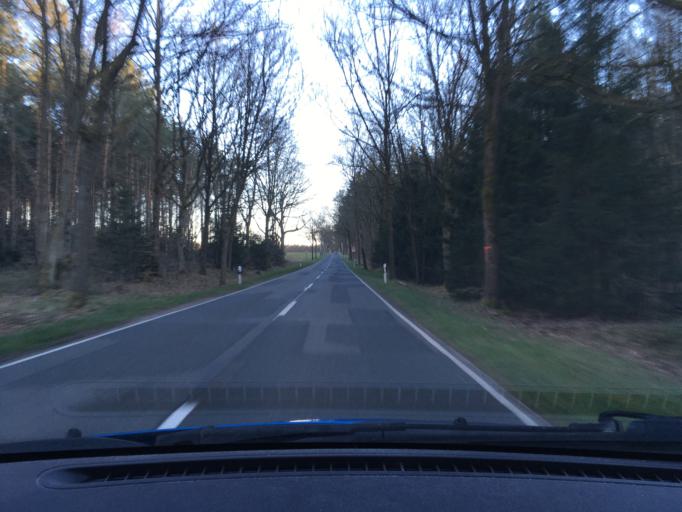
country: DE
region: Lower Saxony
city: Bleckede
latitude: 53.2520
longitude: 10.7456
